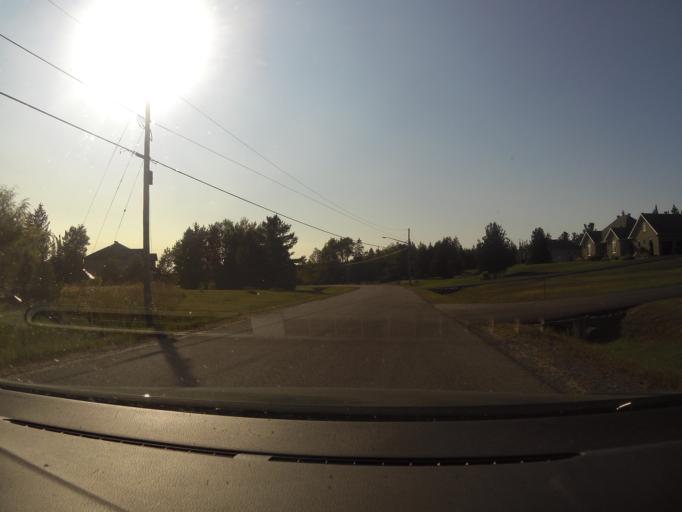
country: CA
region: Ontario
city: Carleton Place
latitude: 45.2898
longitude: -76.1133
